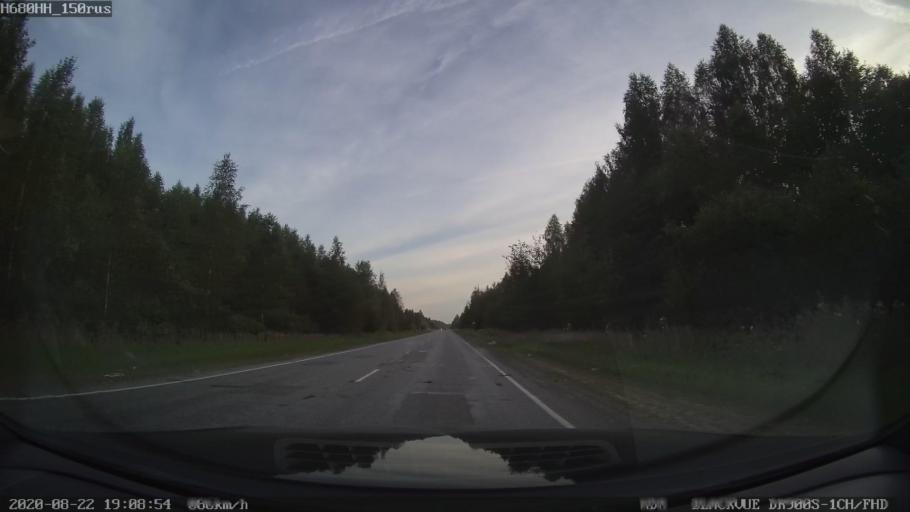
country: RU
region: Tverskaya
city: Sakharovo
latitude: 57.0412
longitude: 36.0737
